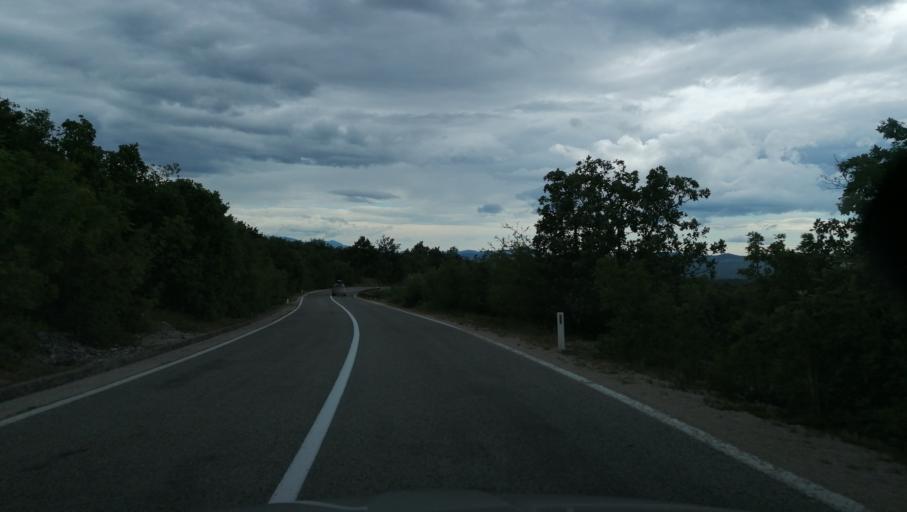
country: BA
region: Republika Srpska
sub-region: Opstina Bileca
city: Bileca
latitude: 43.0019
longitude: 18.4267
